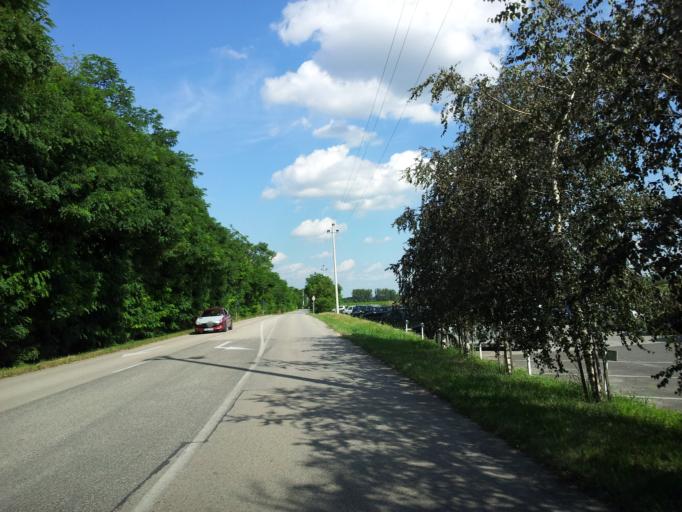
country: HU
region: Pest
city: Szigetcsep
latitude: 47.2624
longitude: 19.0107
